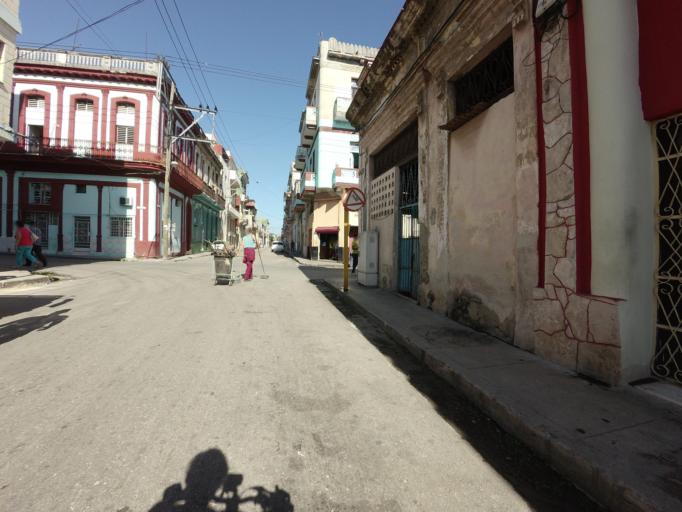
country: CU
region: La Habana
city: Centro Habana
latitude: 23.1352
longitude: -82.3726
